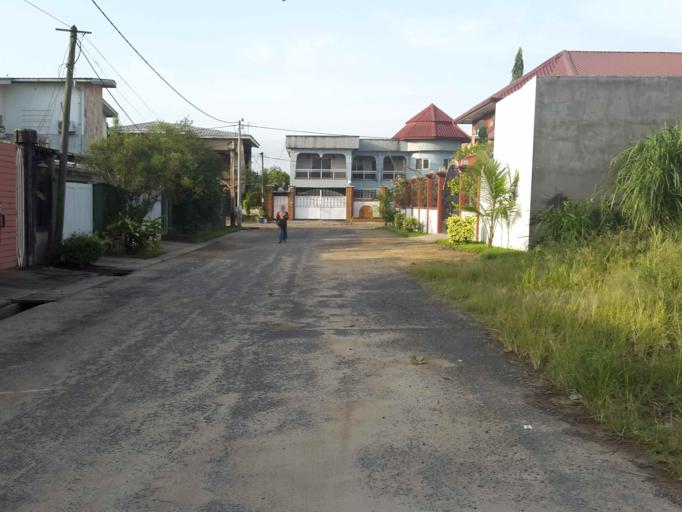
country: CM
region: Littoral
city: Douala
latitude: 4.0914
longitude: 9.7338
